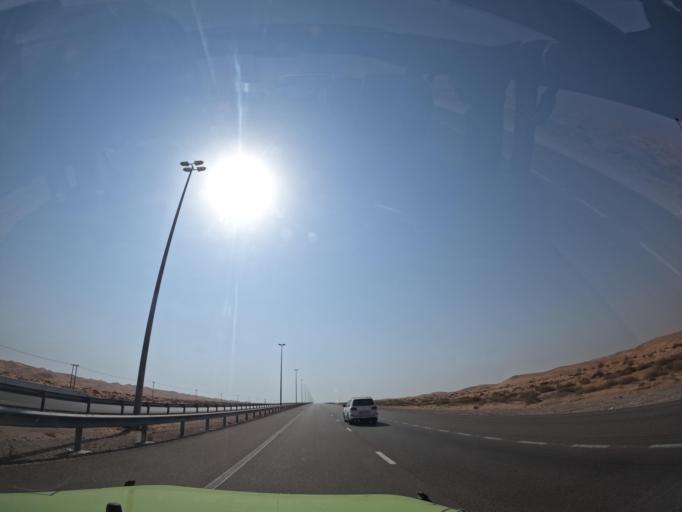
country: OM
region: Al Buraimi
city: Al Buraymi
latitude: 24.4331
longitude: 55.6743
